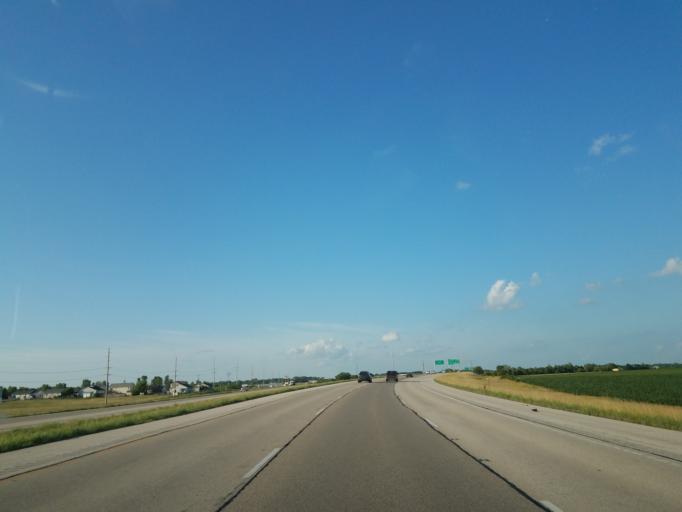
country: US
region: Illinois
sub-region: McLean County
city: Bloomington
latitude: 40.4335
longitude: -89.0311
